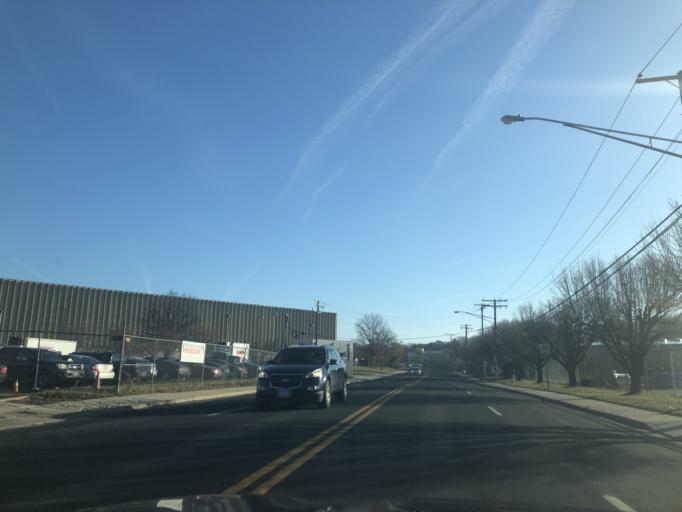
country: US
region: Maryland
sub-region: Prince George's County
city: Landover Hills
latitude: 38.9360
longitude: -76.8801
